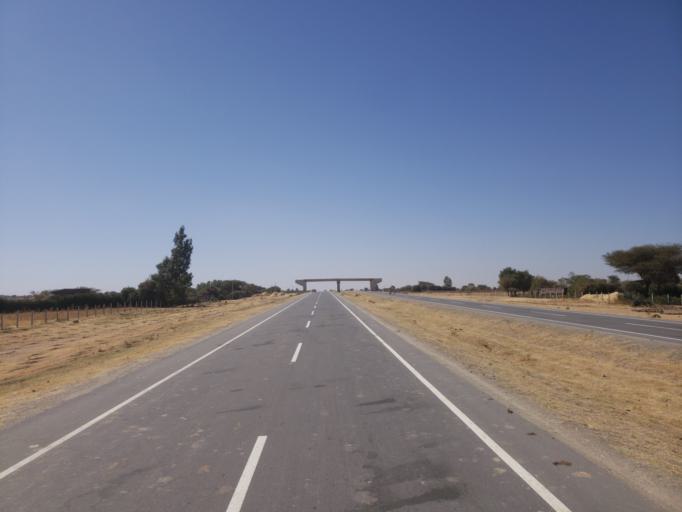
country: ET
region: Oromiya
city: Mojo
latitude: 8.2796
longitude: 38.9143
